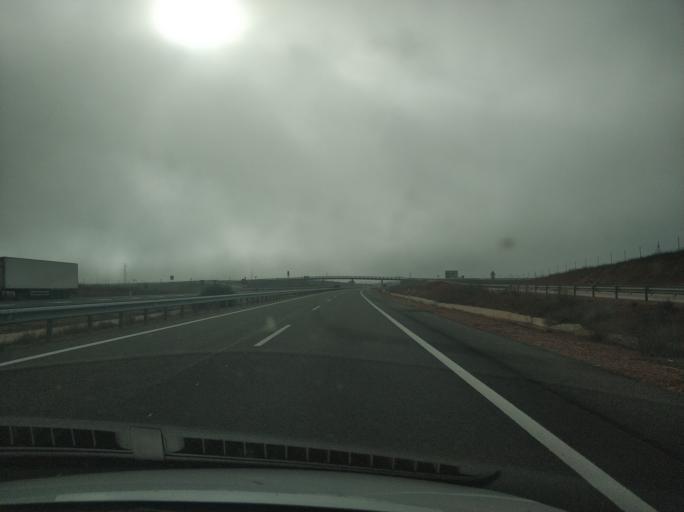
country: ES
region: Castille and Leon
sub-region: Provincia de Soria
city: Alcubilla de las Penas
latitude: 41.2639
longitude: -2.4739
